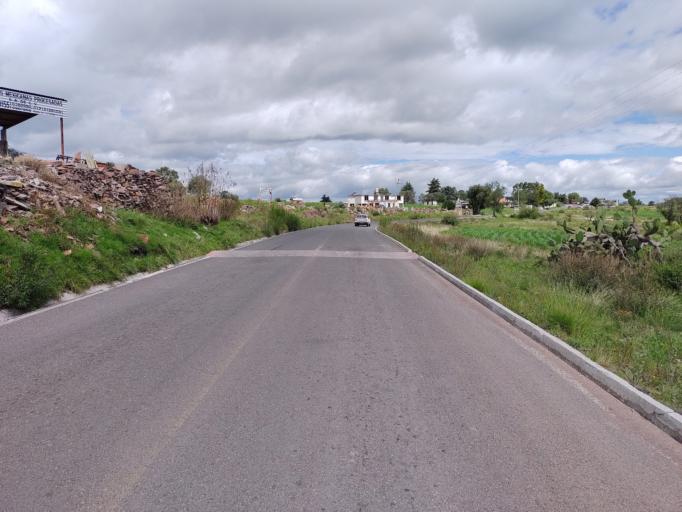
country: MX
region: Mexico
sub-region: Aculco
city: Gunyo Poniente (San Jose Gunyo)
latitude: 20.1138
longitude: -99.8709
